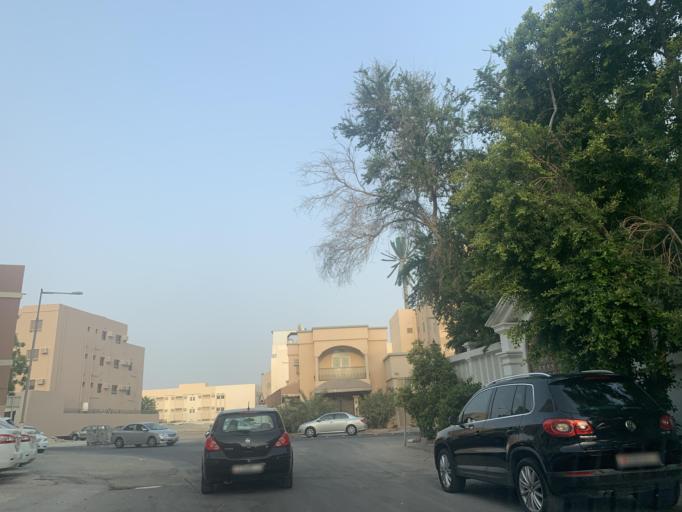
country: BH
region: Manama
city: Jidd Hafs
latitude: 26.2256
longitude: 50.5175
